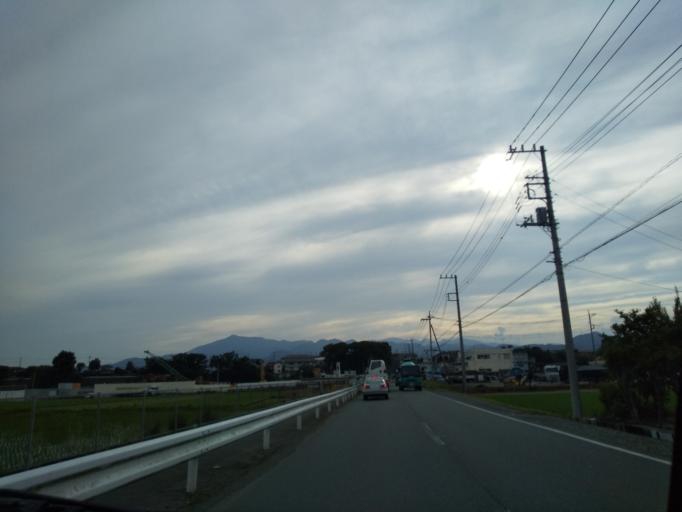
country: JP
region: Kanagawa
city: Zama
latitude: 35.4764
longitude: 139.3552
